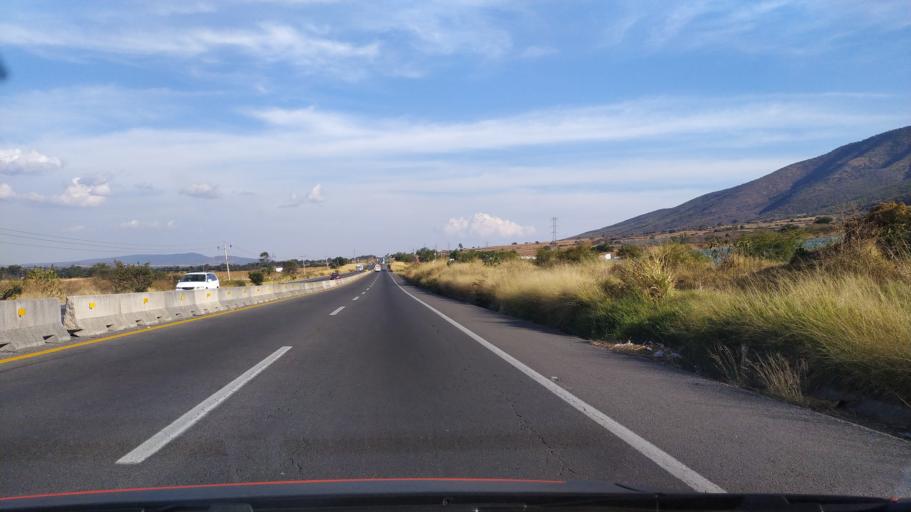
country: MX
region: Jalisco
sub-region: Poncitlan
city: El Romereno (INFONAVIT)
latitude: 20.3978
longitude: -103.0310
